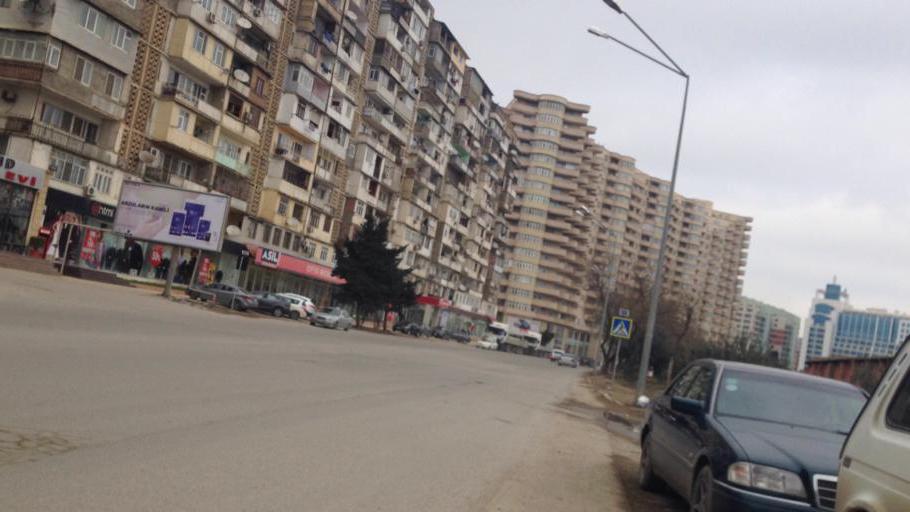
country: AZ
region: Baki
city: Khodzhi-Gasan
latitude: 40.3910
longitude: 49.8150
